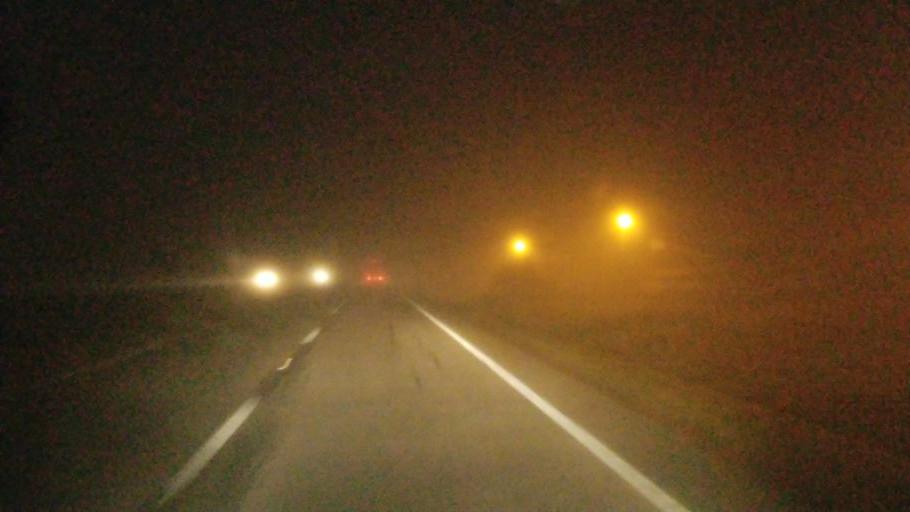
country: US
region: Ohio
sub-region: Pickaway County
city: Logan Elm Village
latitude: 39.5472
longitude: -82.9633
